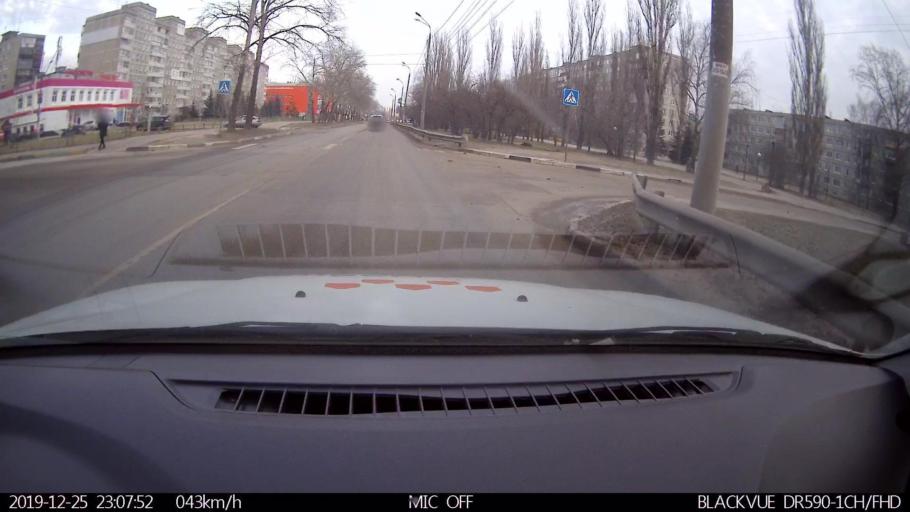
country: RU
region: Nizjnij Novgorod
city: Gorbatovka
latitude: 56.3625
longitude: 43.8113
